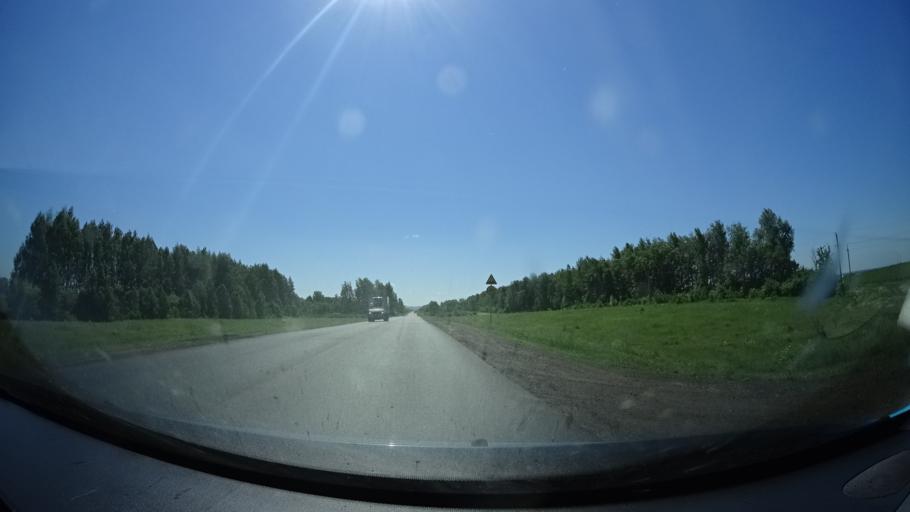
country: RU
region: Bashkortostan
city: Birsk
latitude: 55.2638
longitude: 55.7363
